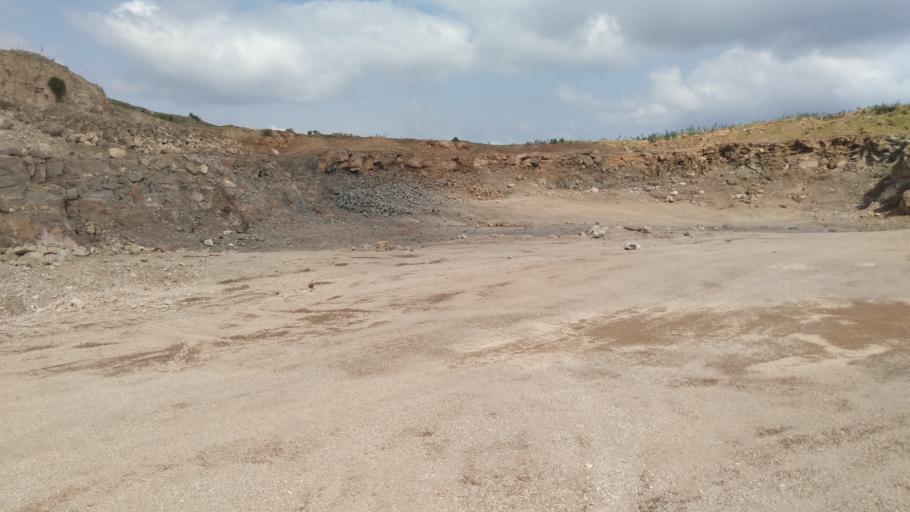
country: ET
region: Oromiya
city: Shashemene
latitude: 7.4503
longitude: 38.6478
